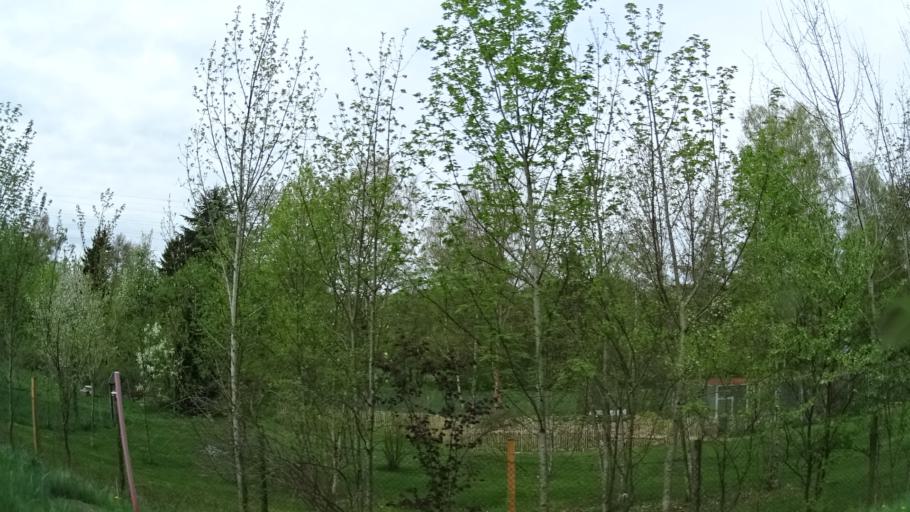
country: DE
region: Baden-Wuerttemberg
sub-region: Freiburg Region
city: Monchweiler
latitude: 48.0820
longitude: 8.4533
